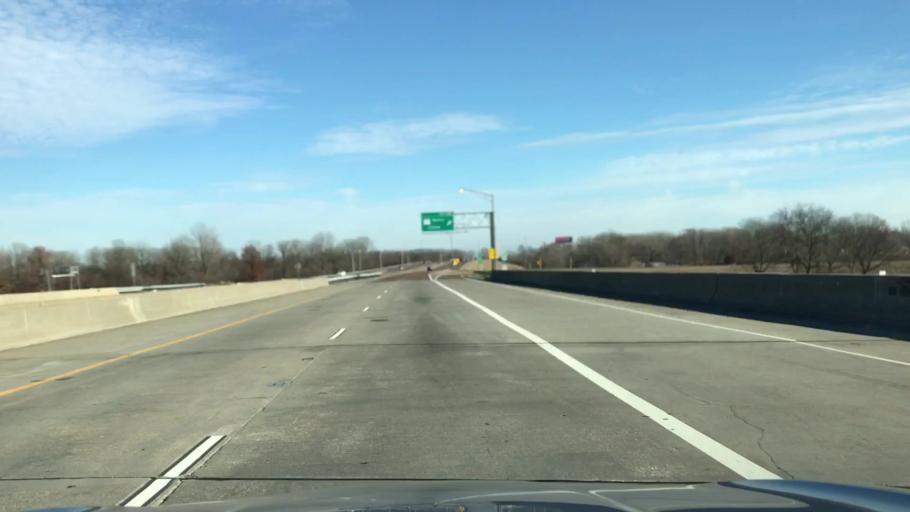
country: US
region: Illinois
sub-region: Madison County
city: Mitchell
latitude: 38.7660
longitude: -90.1245
